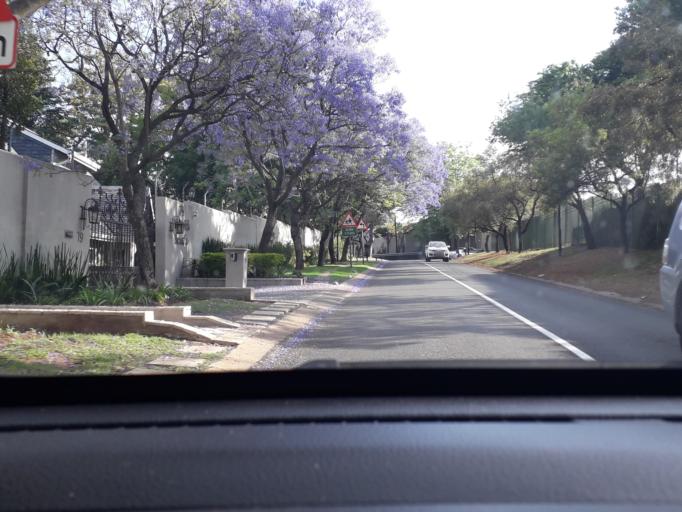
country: ZA
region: Gauteng
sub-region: City of Johannesburg Metropolitan Municipality
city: Modderfontein
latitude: -26.0812
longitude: 28.0583
